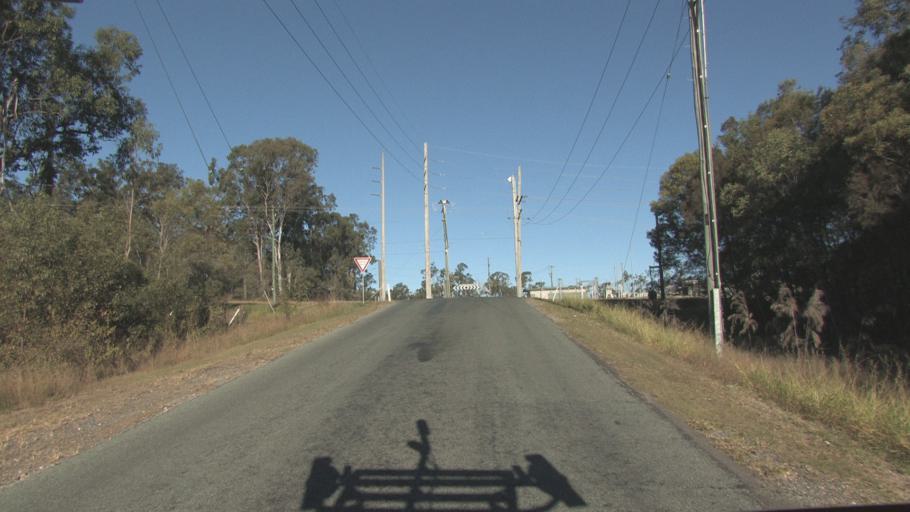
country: AU
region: Queensland
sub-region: Logan
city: North Maclean
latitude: -27.8080
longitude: 153.0439
